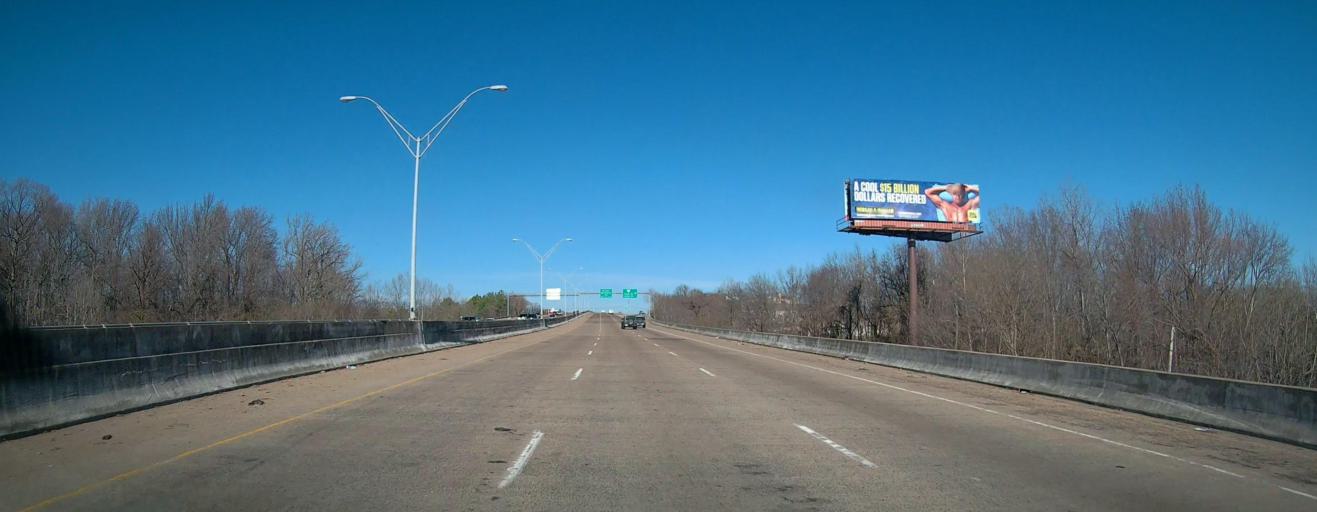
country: US
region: Tennessee
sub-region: Shelby County
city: Bartlett
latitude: 35.2000
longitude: -89.9246
